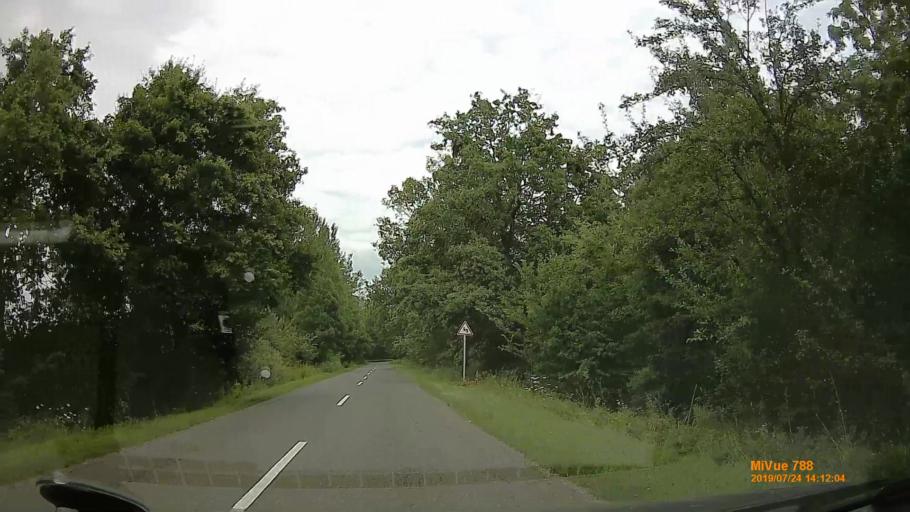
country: UA
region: Zakarpattia
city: Batiovo
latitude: 48.3214
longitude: 22.3060
